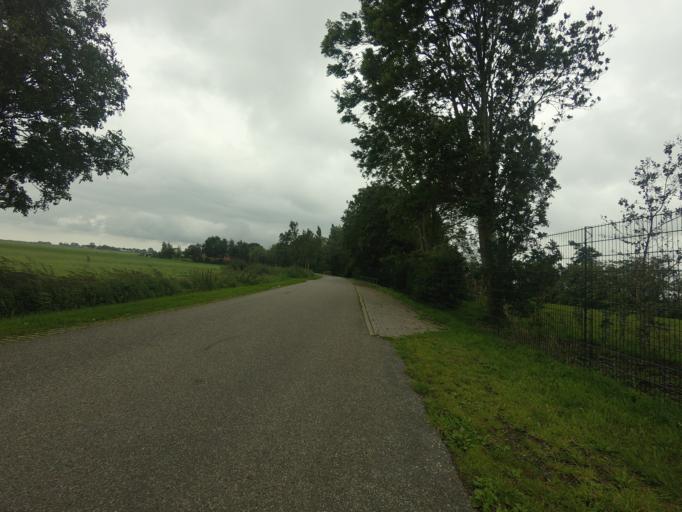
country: NL
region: Friesland
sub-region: Sudwest Fryslan
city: Bolsward
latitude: 52.9973
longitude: 5.5449
